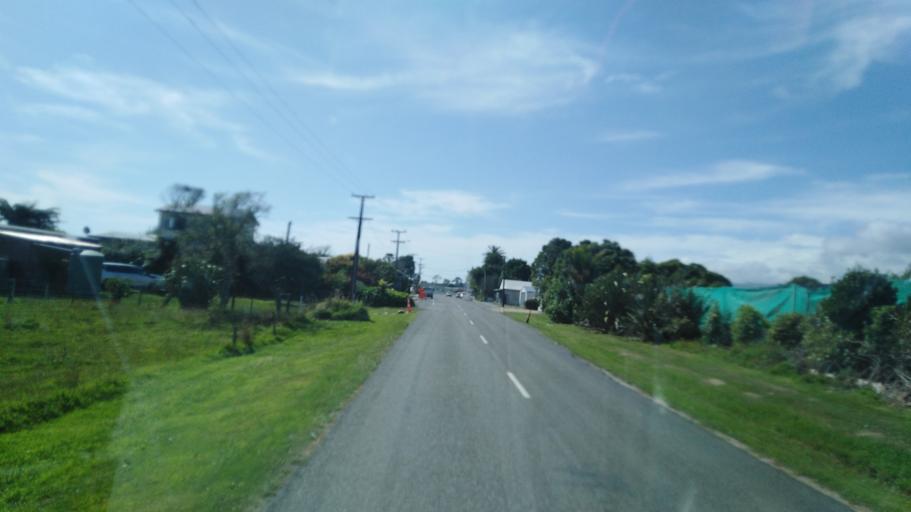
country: NZ
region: West Coast
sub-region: Buller District
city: Westport
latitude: -41.2533
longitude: 172.1295
